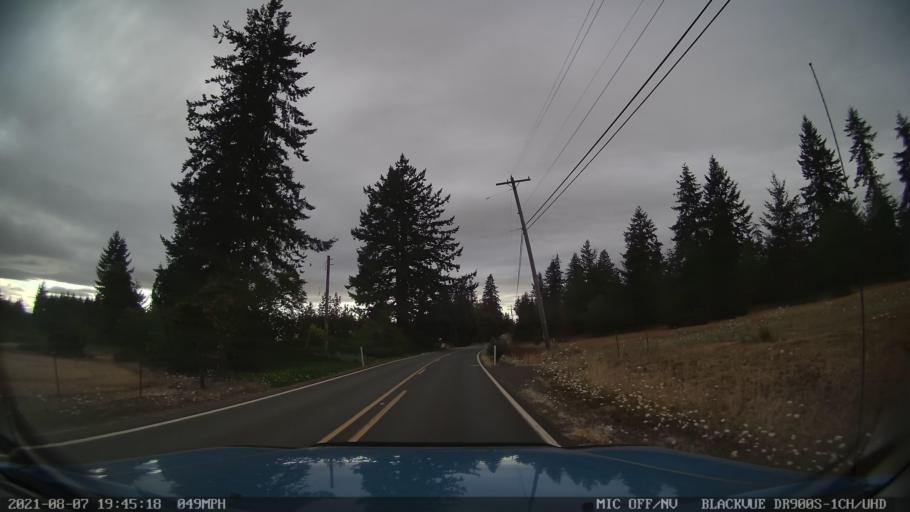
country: US
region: Oregon
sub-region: Marion County
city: Silverton
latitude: 44.9469
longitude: -122.6942
